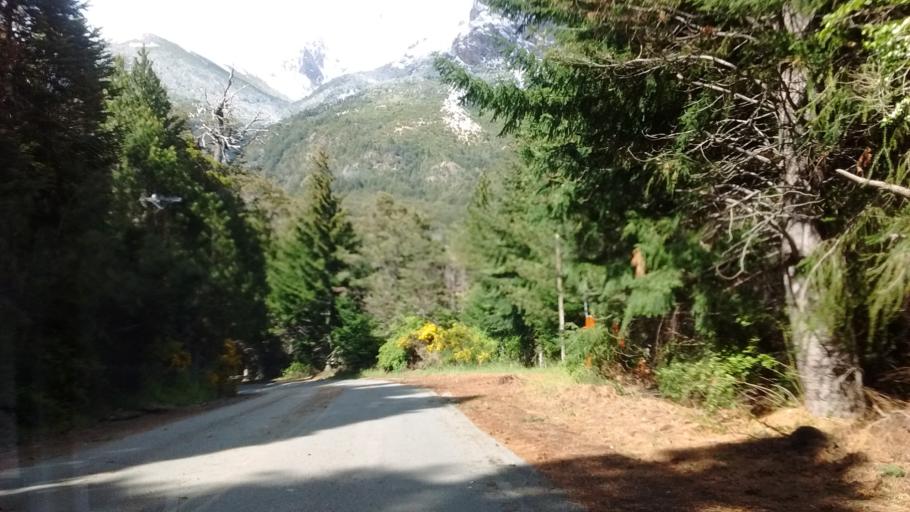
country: AR
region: Rio Negro
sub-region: Departamento de Bariloche
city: San Carlos de Bariloche
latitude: -41.0761
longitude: -71.5456
